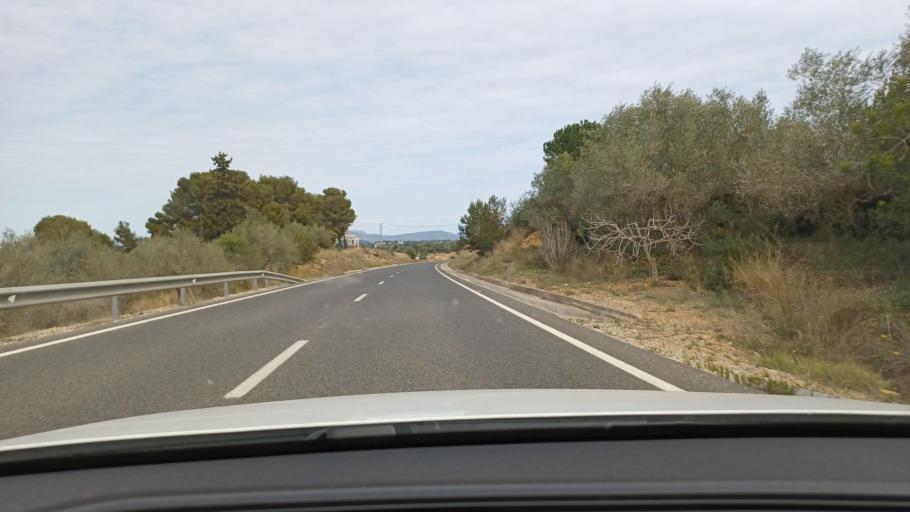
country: ES
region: Catalonia
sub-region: Provincia de Tarragona
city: Masdenverge
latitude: 40.6876
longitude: 0.5282
